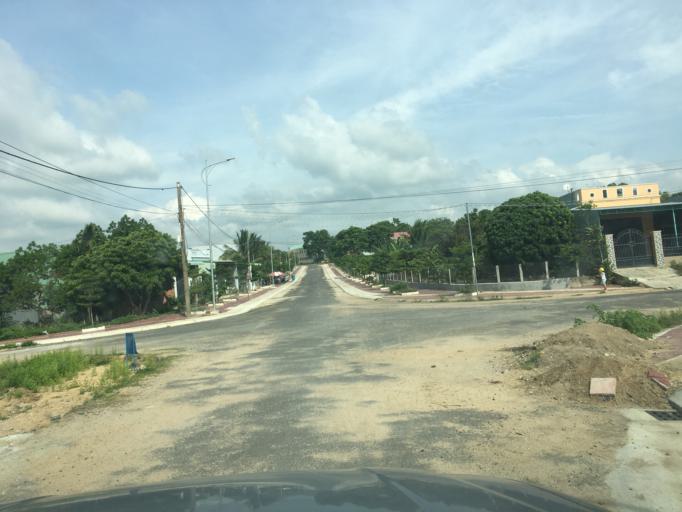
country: VN
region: Gia Lai
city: Kong Chro
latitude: 13.7734
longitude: 108.5268
